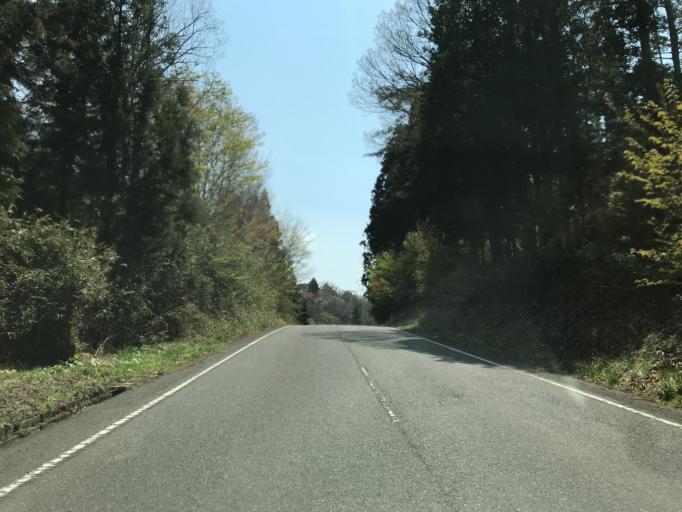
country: JP
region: Fukushima
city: Ishikawa
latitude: 37.0964
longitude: 140.4083
